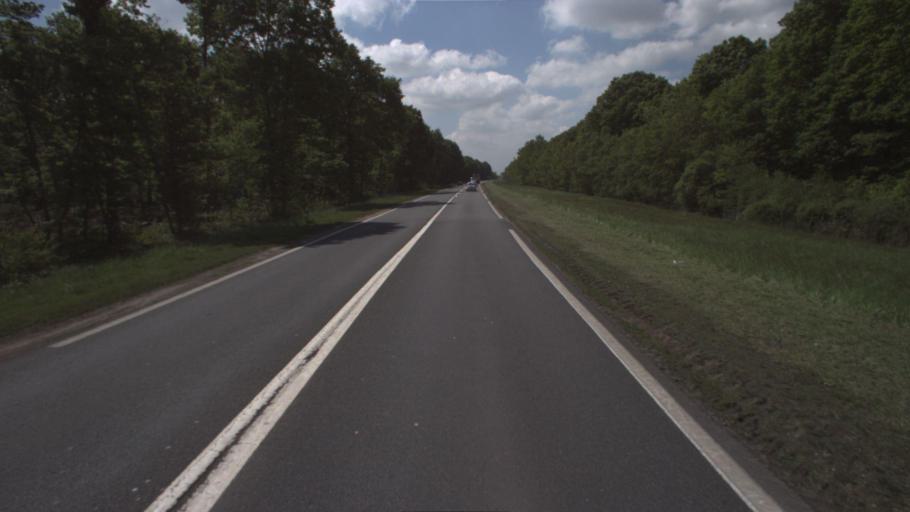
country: FR
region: Ile-de-France
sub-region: Departement de Seine-et-Marne
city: Guignes
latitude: 48.6510
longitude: 2.8035
